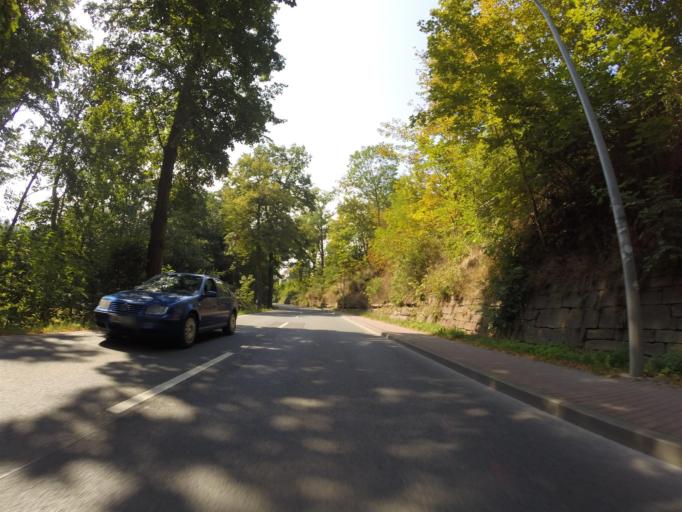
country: DE
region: Thuringia
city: Stadtroda
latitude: 50.8672
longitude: 11.7222
